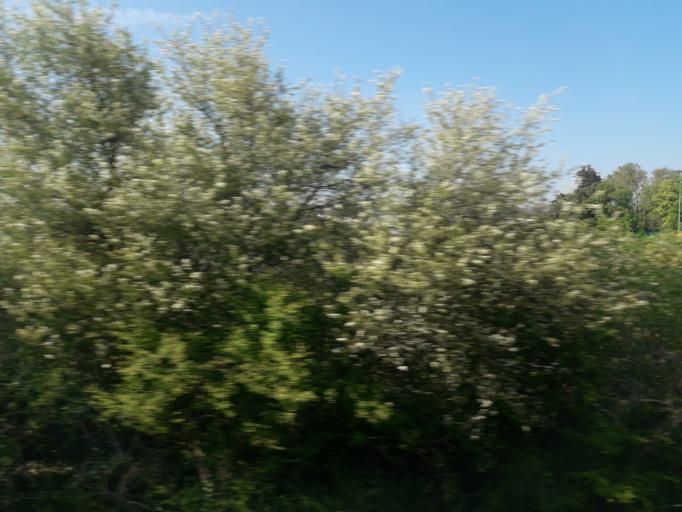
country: FR
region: Rhone-Alpes
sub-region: Departement de la Drome
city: Romans-sur-Isere
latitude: 45.0530
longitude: 5.0821
